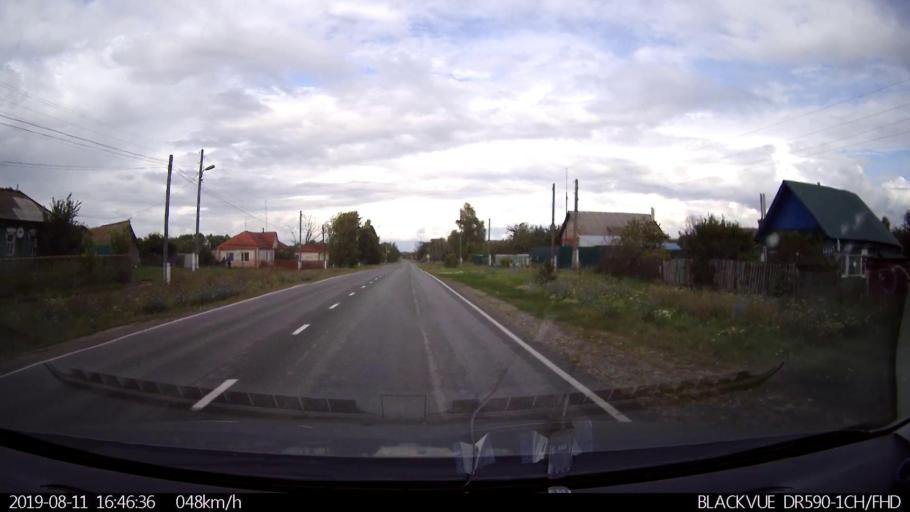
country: RU
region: Ulyanovsk
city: Mayna
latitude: 54.1987
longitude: 47.6899
